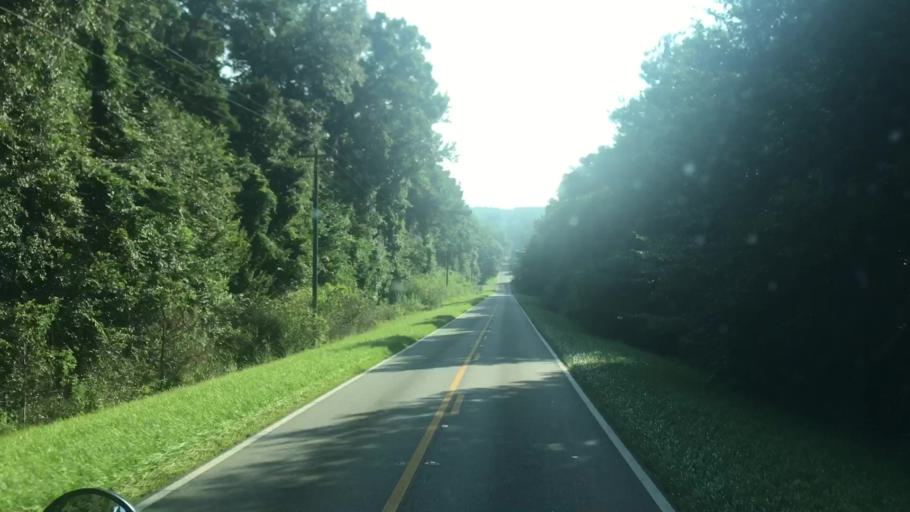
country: US
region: Florida
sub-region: Gadsden County
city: Quincy
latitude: 30.6643
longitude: -84.5560
